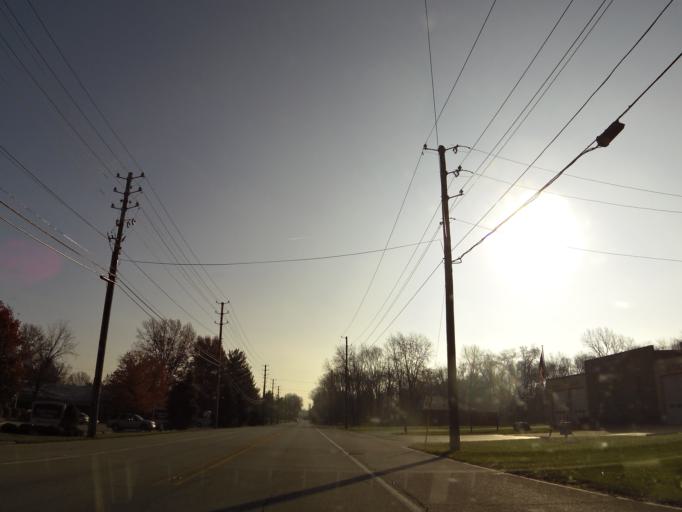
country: US
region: Indiana
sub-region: Marion County
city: Clermont
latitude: 39.8086
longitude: -86.3025
